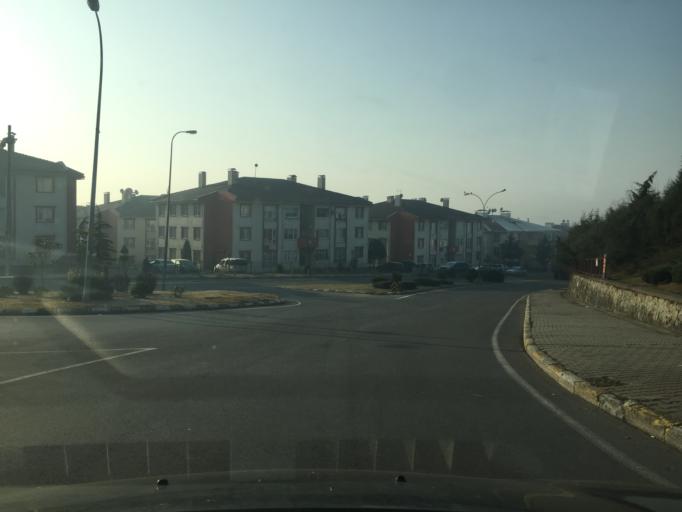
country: TR
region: Duzce
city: Duzce
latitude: 40.8567
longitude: 31.2286
